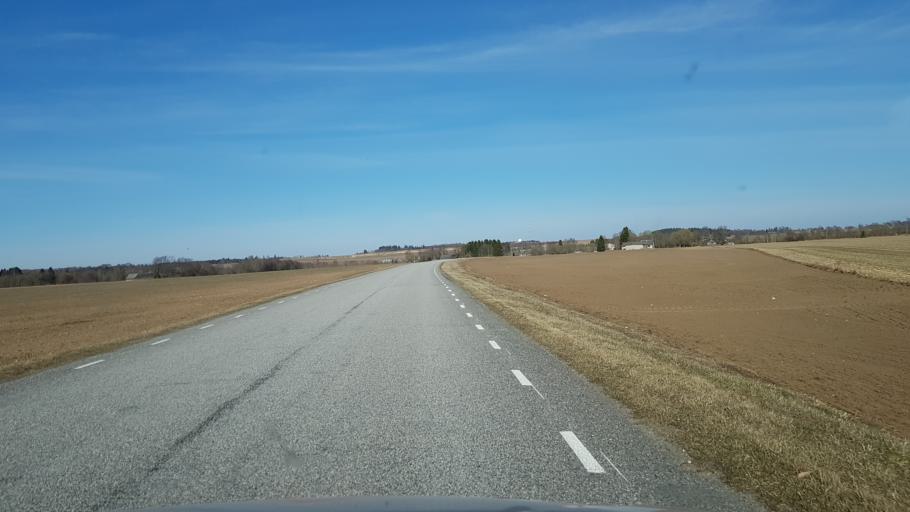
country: EE
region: Laeaene-Virumaa
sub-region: Vaeike-Maarja vald
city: Vaike-Maarja
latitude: 59.0620
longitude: 26.4723
